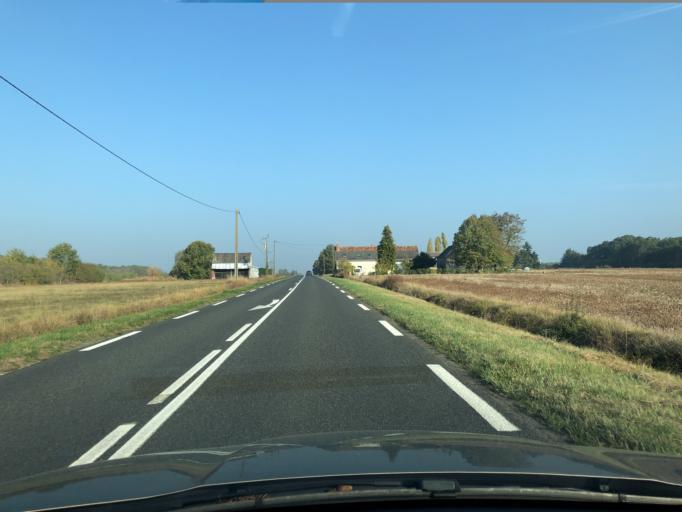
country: FR
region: Centre
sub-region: Departement d'Indre-et-Loire
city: Cerelles
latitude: 47.5050
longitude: 0.6965
